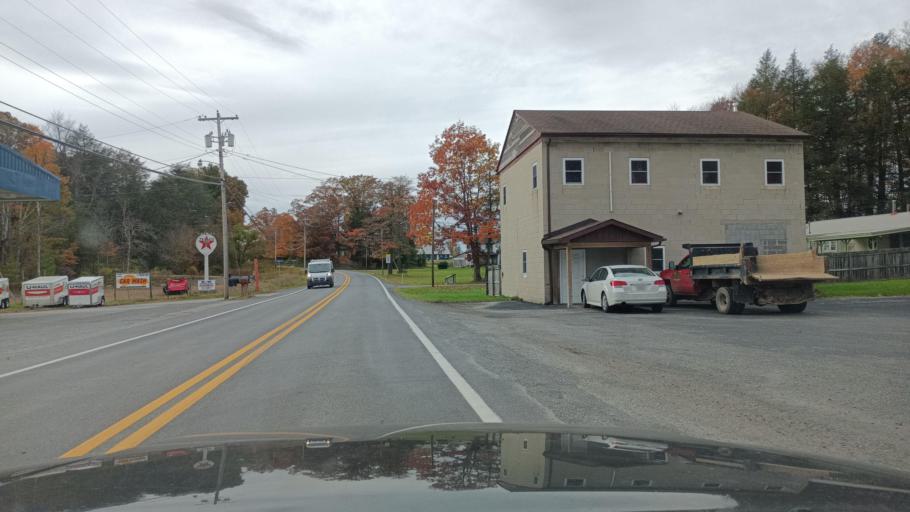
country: US
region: West Virginia
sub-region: Preston County
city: Terra Alta
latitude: 39.3248
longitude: -79.5474
